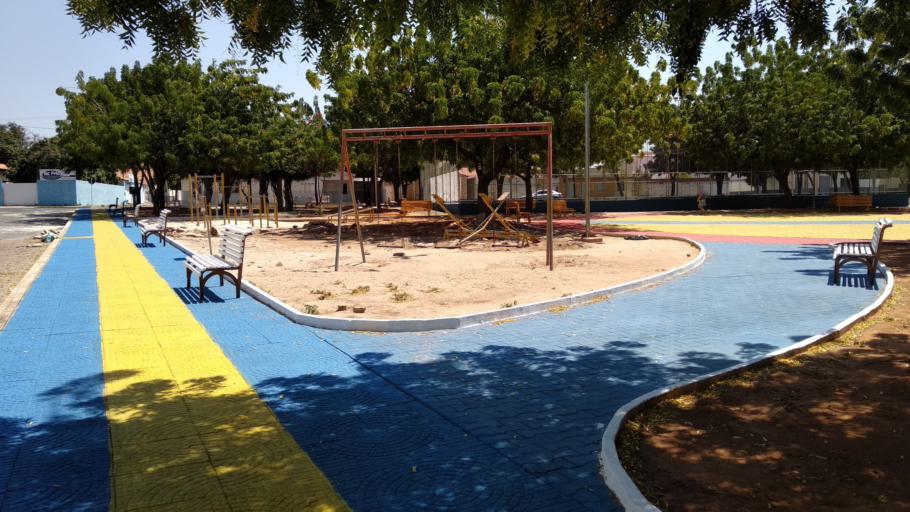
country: BR
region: Bahia
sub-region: Guanambi
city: Guanambi
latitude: -14.2162
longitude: -42.7807
